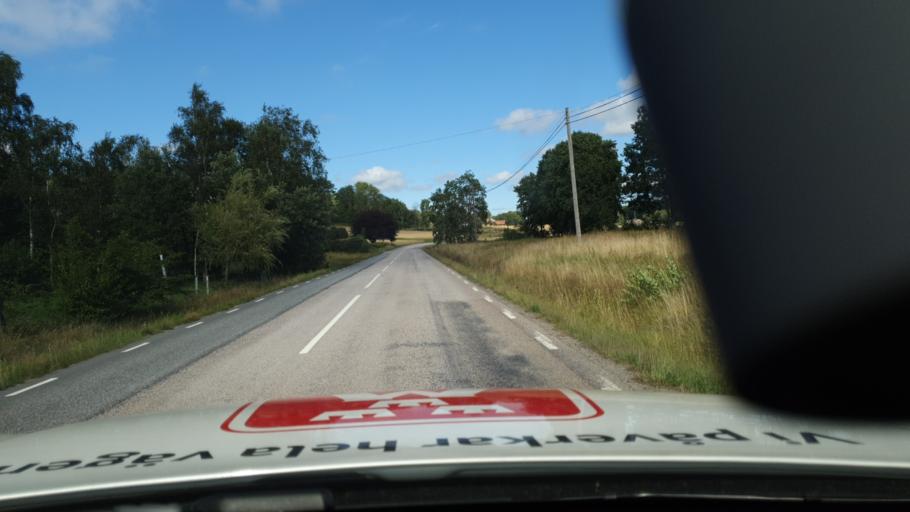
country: SE
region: Vaestra Goetaland
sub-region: Orust
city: Henan
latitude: 58.2218
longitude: 11.6125
